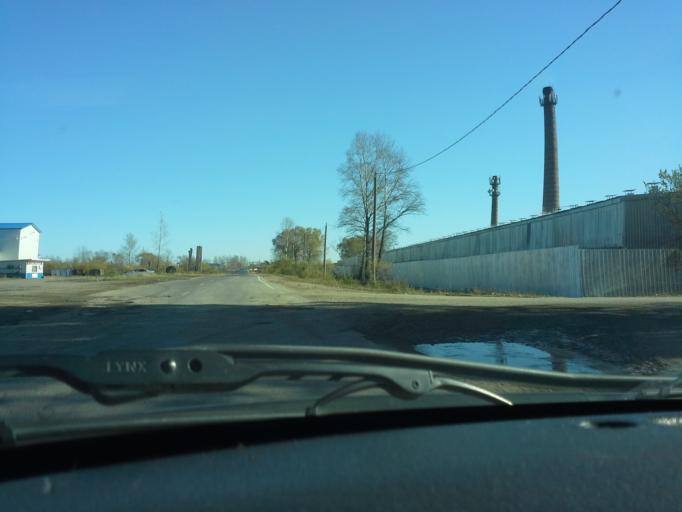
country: RU
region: Jewish Autonomous Oblast
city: Priamurskiy
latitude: 48.5353
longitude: 134.9020
